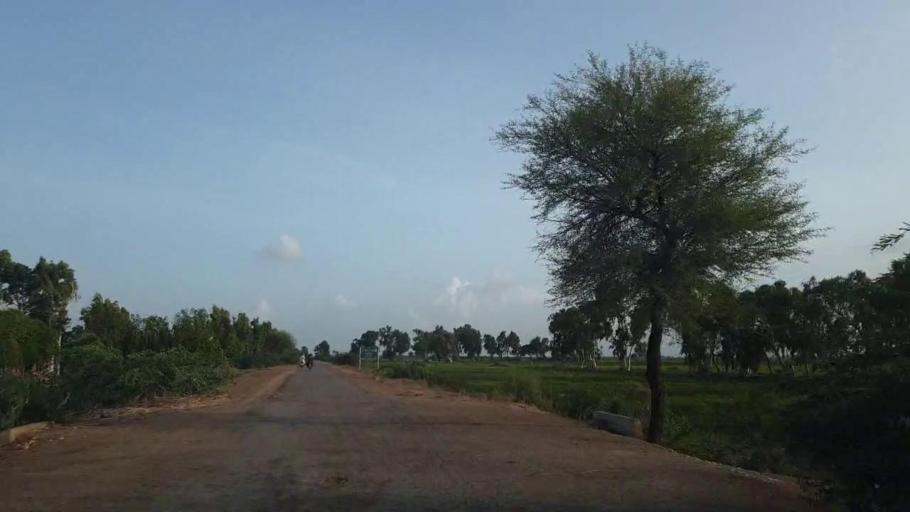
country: PK
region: Sindh
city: Kadhan
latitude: 24.6164
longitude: 69.1158
